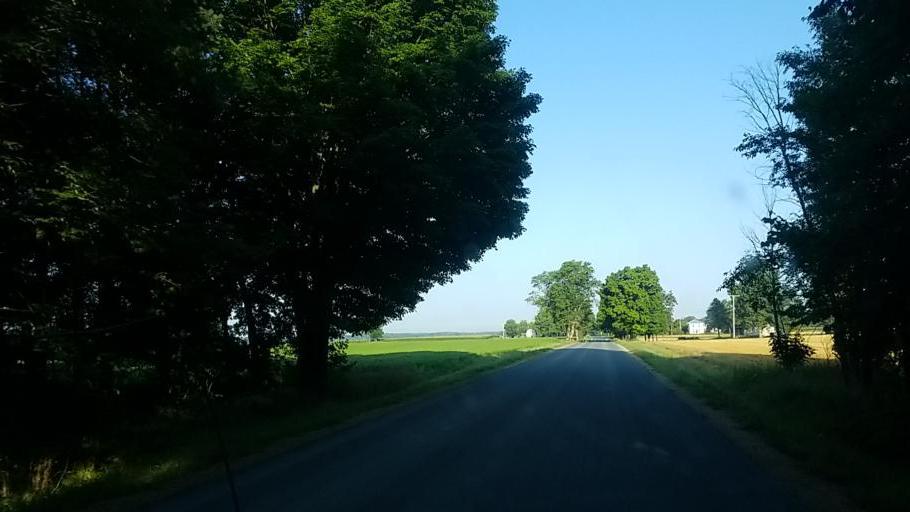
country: US
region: Michigan
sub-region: Montcalm County
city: Howard City
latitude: 43.3670
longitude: -85.4571
